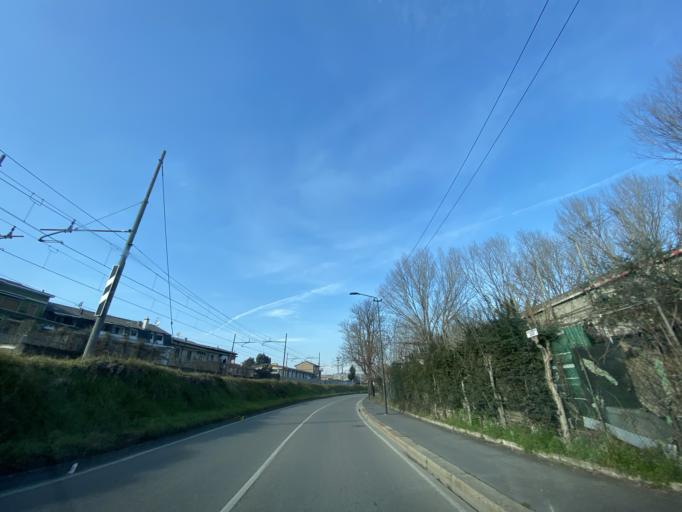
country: IT
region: Lombardy
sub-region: Citta metropolitana di Milano
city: Novate Milanese
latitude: 45.5045
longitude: 9.1480
